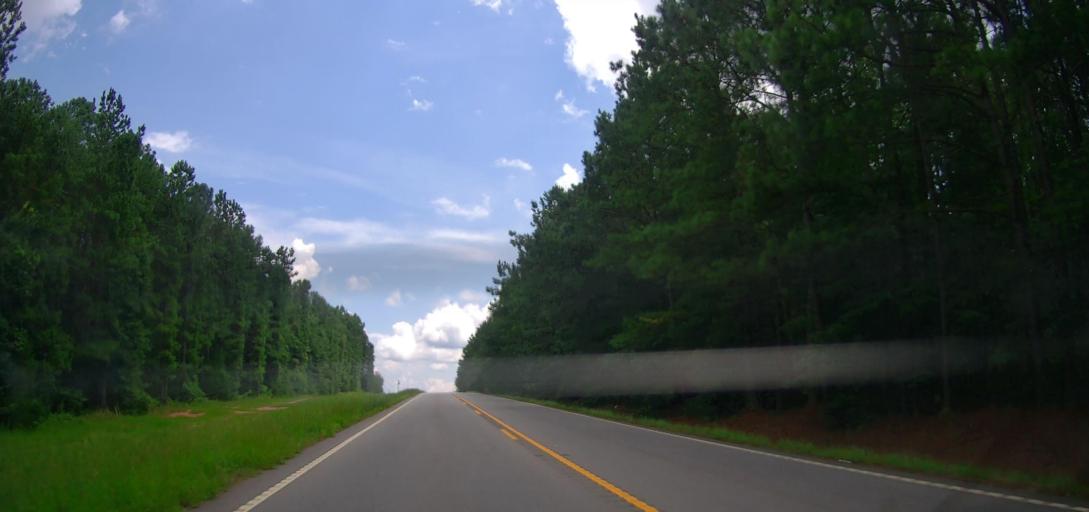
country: US
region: Georgia
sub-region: Meriwether County
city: Greenville
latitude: 32.9908
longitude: -84.6241
